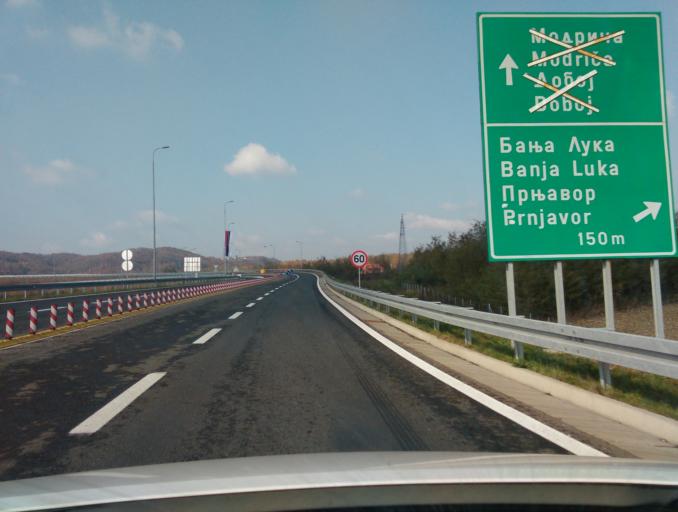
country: BA
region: Republika Srpska
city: Doboj
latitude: 44.8104
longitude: 18.0455
